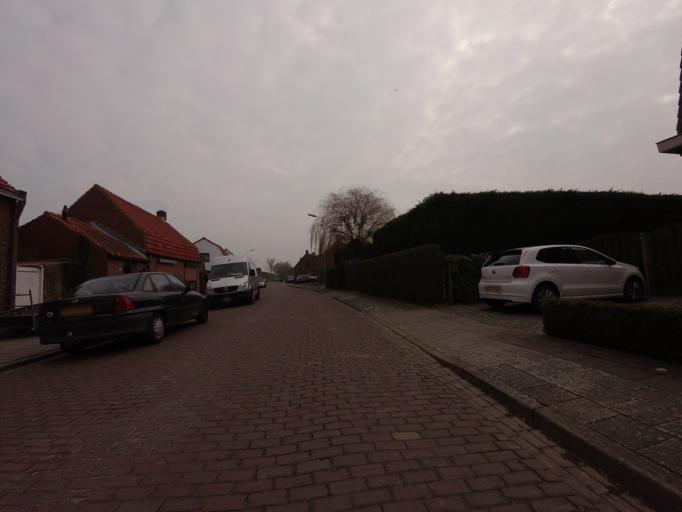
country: NL
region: Zeeland
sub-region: Gemeente Hulst
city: Hulst
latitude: 51.3530
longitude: 4.1076
